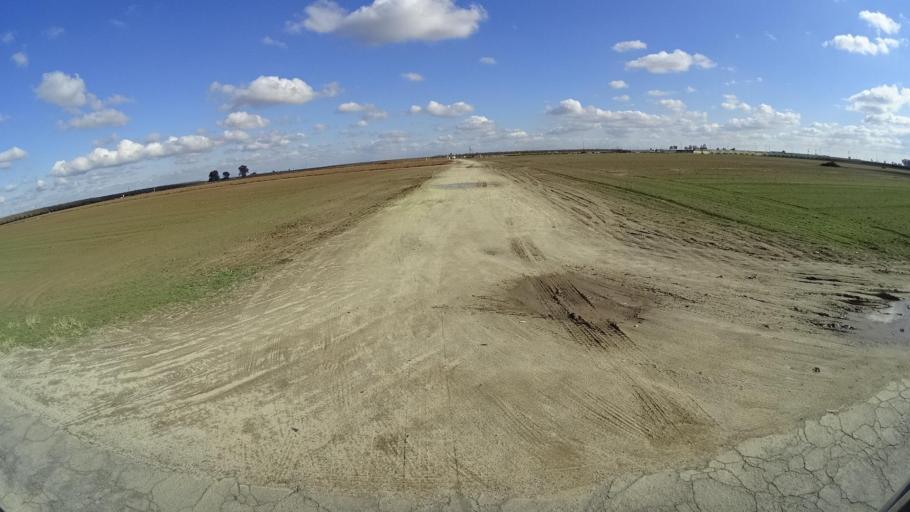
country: US
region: California
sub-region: Kern County
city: Delano
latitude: 35.7432
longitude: -119.3478
